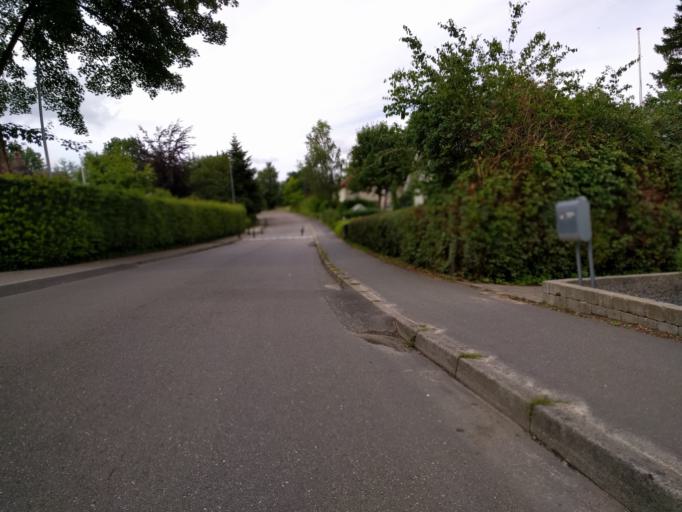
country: DK
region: Central Jutland
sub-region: Skanderborg Kommune
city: Ry
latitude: 56.0855
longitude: 9.7635
